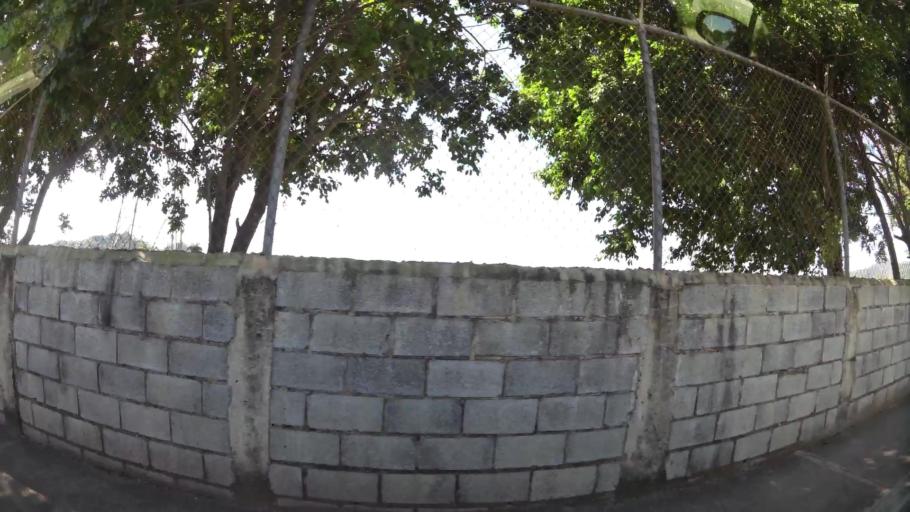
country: DO
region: San Cristobal
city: San Cristobal
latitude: 18.4258
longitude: -70.1285
